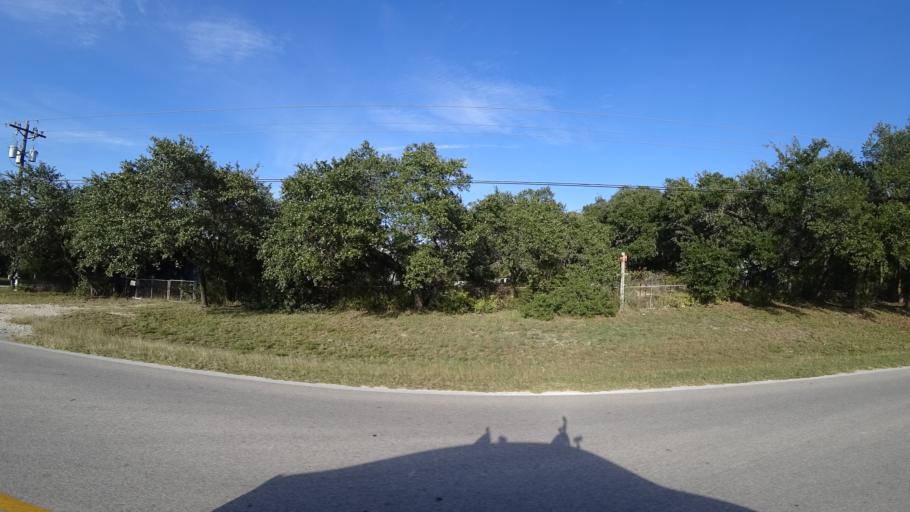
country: US
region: Texas
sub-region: Travis County
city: Barton Creek
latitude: 30.2377
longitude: -97.9169
